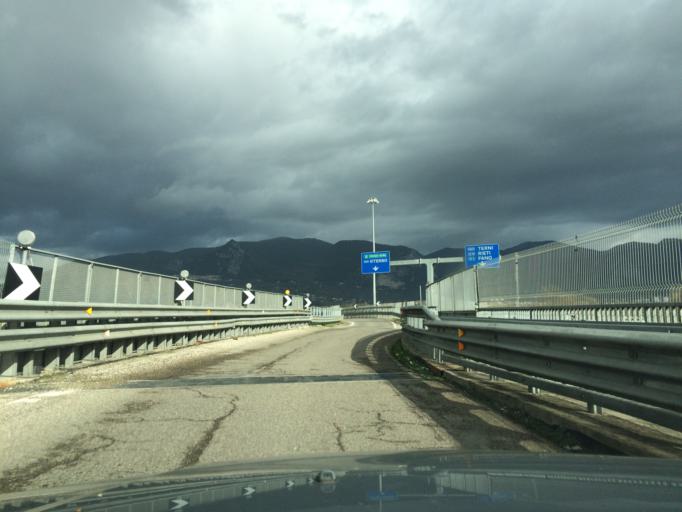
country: IT
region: Umbria
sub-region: Provincia di Terni
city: San Gemini
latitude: 42.5681
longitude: 12.5777
